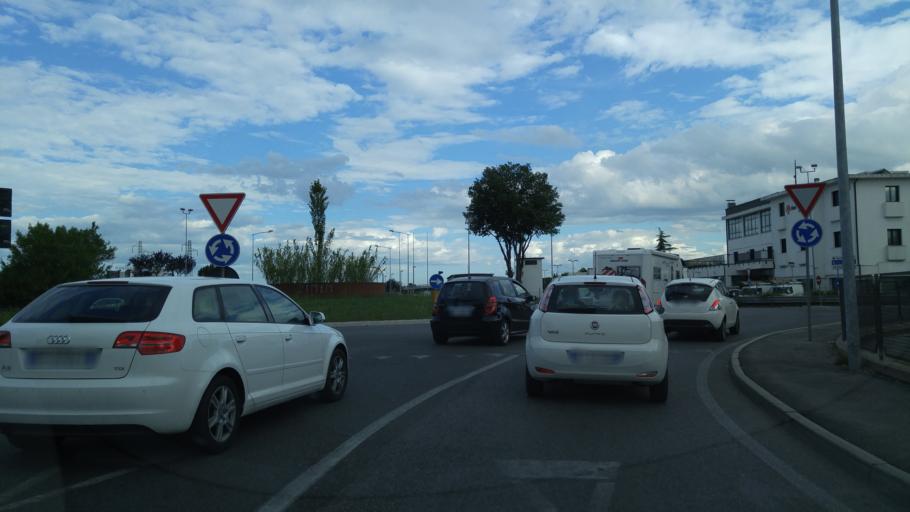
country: IT
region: Emilia-Romagna
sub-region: Provincia di Rimini
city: Rimini
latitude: 44.0464
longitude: 12.5523
